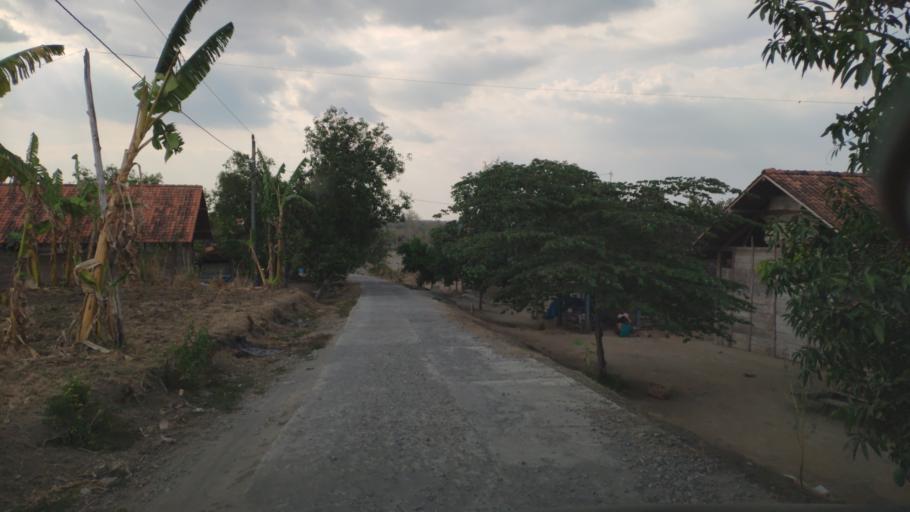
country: ID
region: Central Java
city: Randublatung
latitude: -7.2915
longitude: 111.3166
